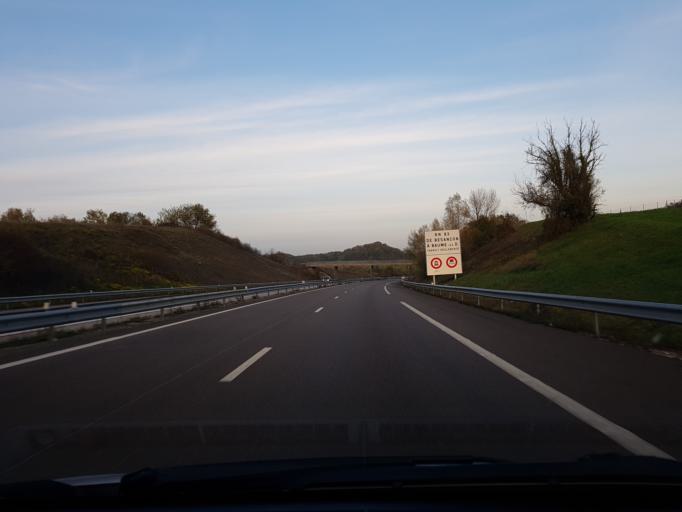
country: FR
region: Franche-Comte
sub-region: Departement du Doubs
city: Dannemarie-sur-Crete
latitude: 47.2176
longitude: 5.8624
